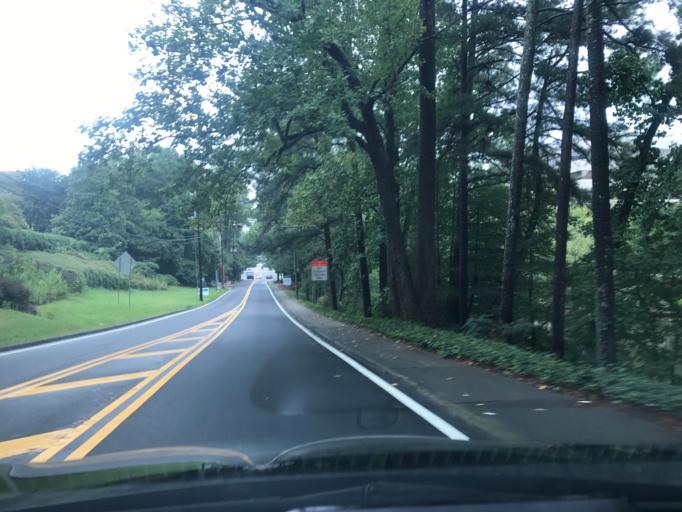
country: US
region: Georgia
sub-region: Fulton County
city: Sandy Springs
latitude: 33.9126
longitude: -84.3520
